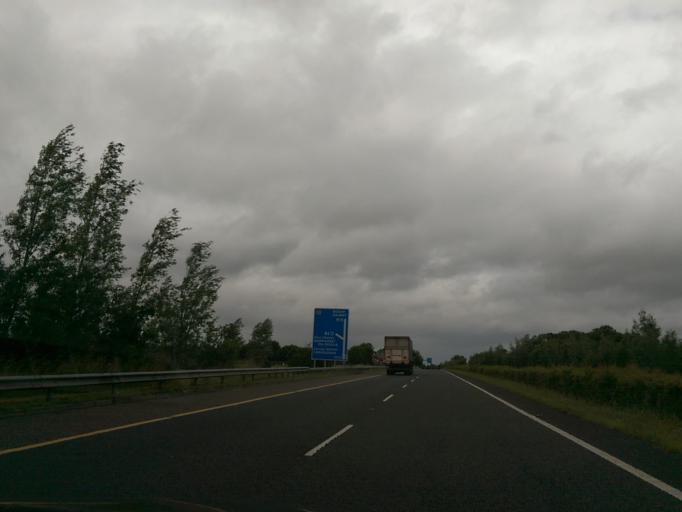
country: IE
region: Munster
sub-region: An Clar
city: Newmarket on Fergus
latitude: 52.7413
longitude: -8.8933
